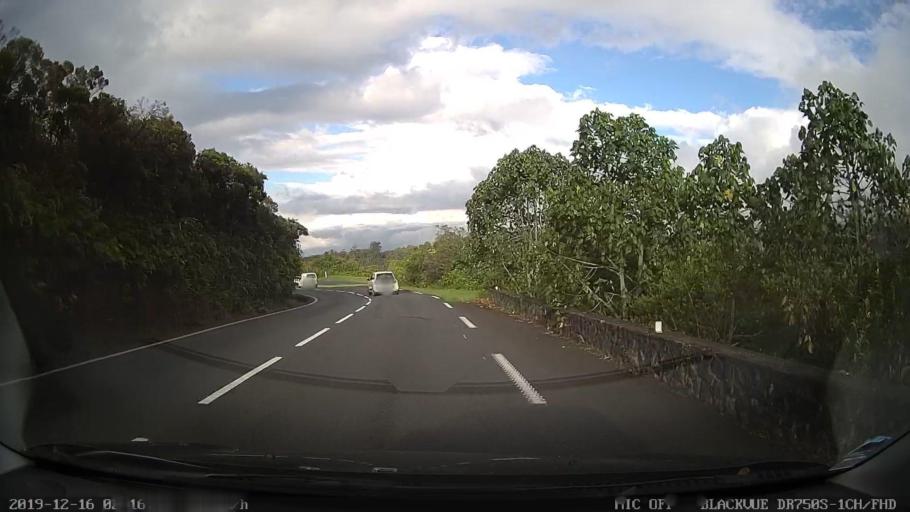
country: RE
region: Reunion
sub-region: Reunion
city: Cilaos
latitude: -21.1555
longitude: 55.6017
